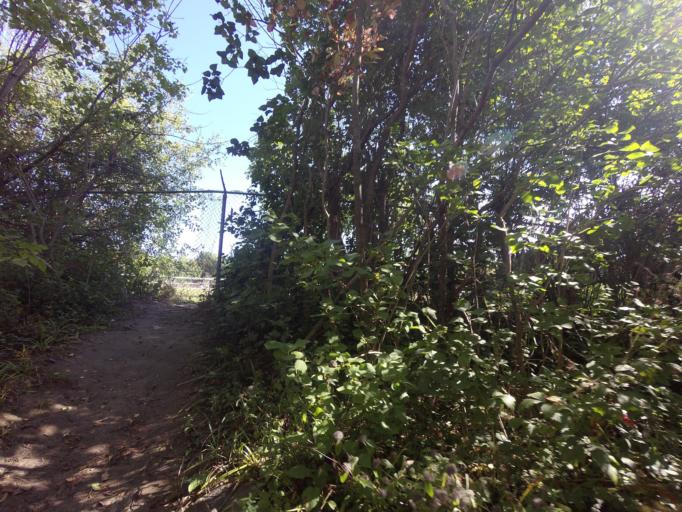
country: CA
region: Ontario
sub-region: Wellington County
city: Guelph
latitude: 43.6814
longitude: -80.4383
